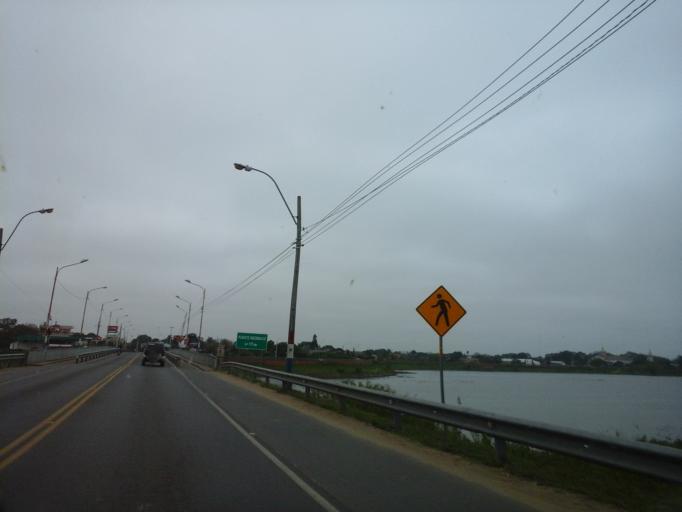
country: PY
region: Neembucu
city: Pilar
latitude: -26.8523
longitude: -58.2955
